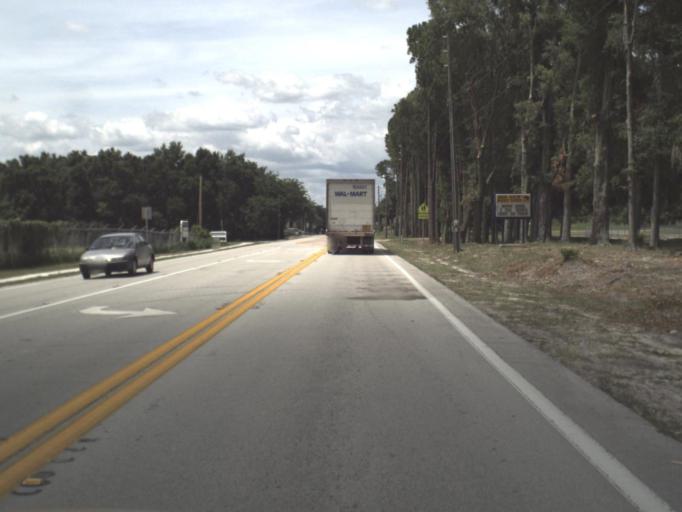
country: US
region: Florida
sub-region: Alachua County
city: Newberry
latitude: 29.6405
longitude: -82.6066
